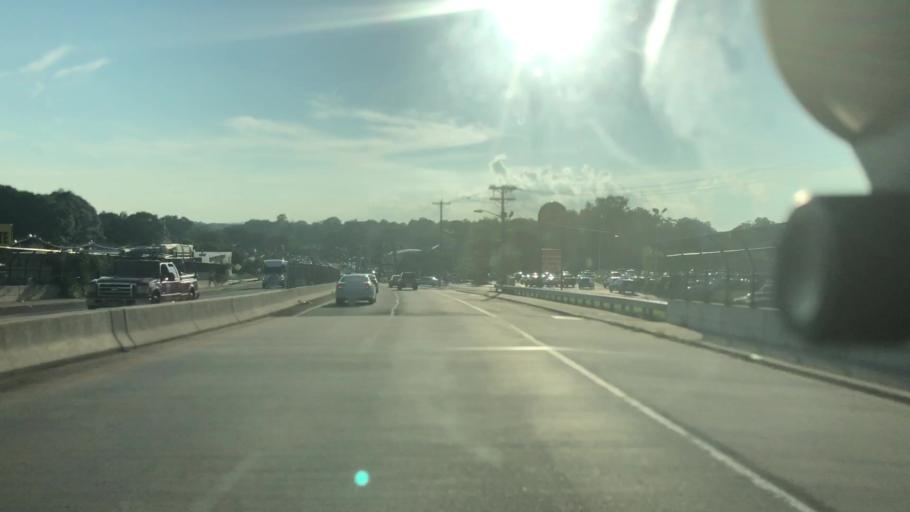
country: US
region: New Jersey
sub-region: Union County
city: Hillside
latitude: 40.6994
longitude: -74.2327
